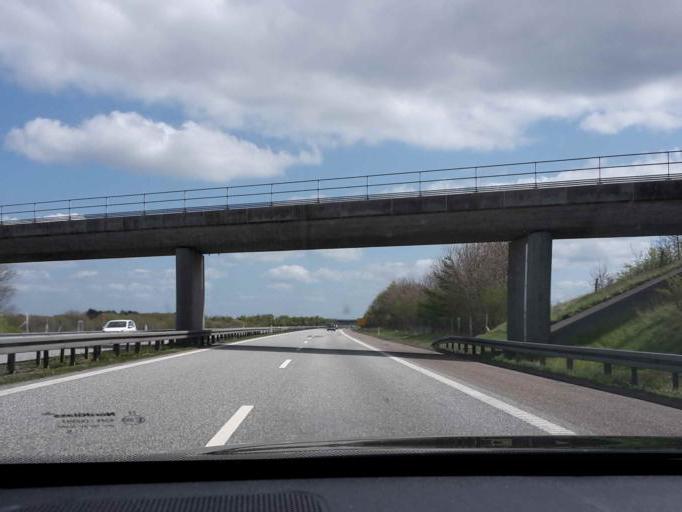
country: DK
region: South Denmark
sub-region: Esbjerg Kommune
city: Bramming
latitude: 55.5144
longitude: 8.7787
